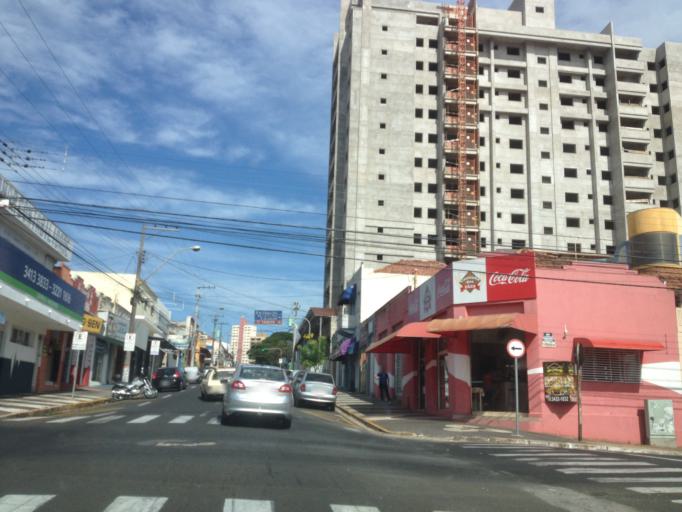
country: BR
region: Sao Paulo
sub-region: Marilia
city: Marilia
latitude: -22.2148
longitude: -49.9435
